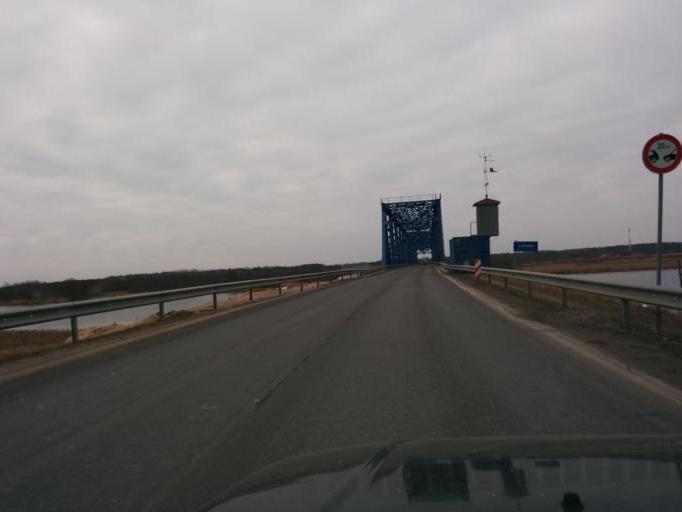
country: LV
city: Tireli
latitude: 56.8359
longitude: 23.5769
